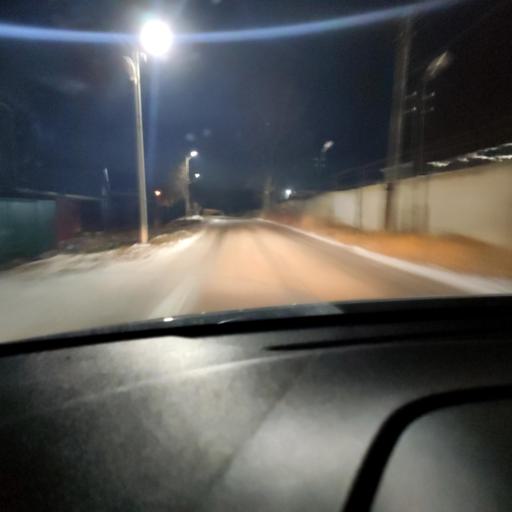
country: RU
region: Tatarstan
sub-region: Gorod Kazan'
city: Kazan
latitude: 55.7226
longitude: 49.0985
